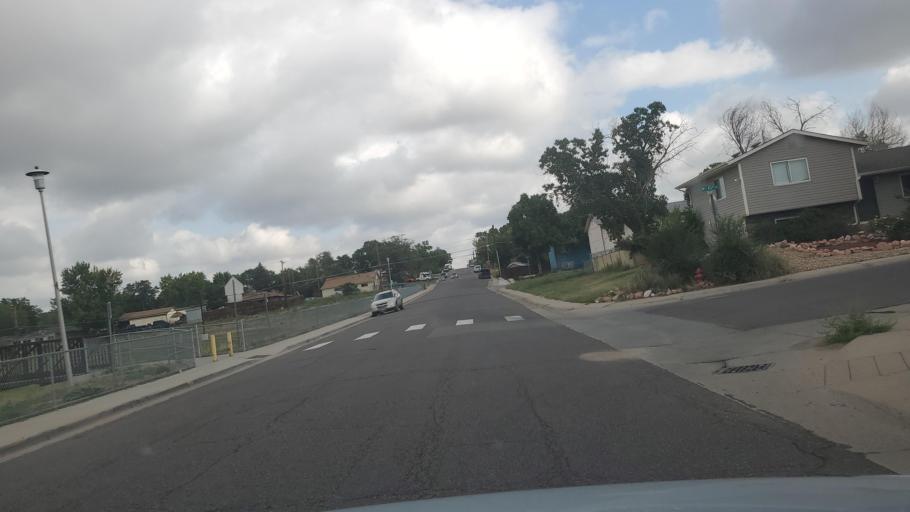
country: US
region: Colorado
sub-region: Adams County
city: Welby
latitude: 39.8477
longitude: -104.9684
